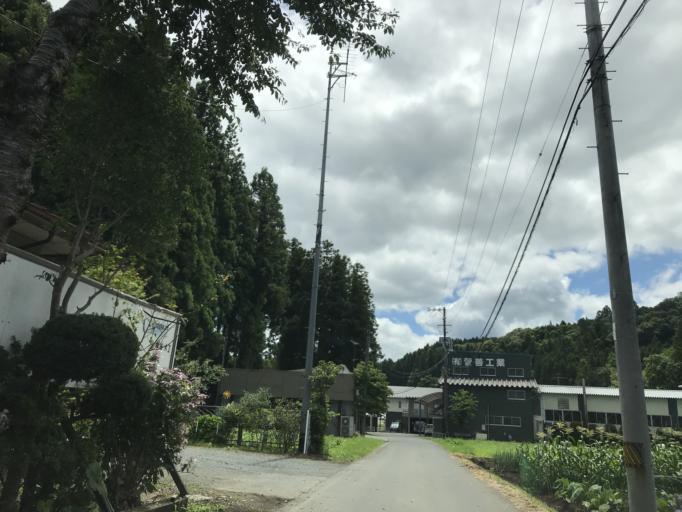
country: JP
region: Iwate
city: Ichinoseki
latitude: 38.9324
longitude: 141.0795
